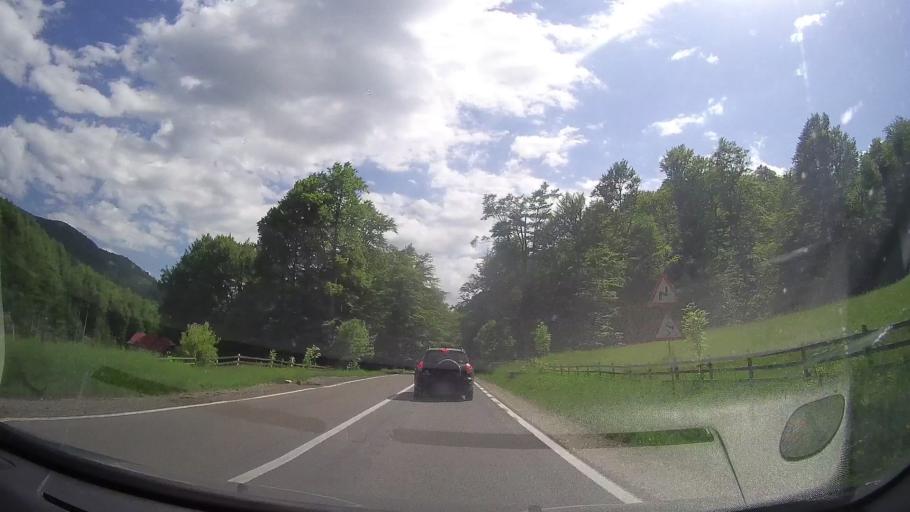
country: RO
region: Prahova
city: Maneciu
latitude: 45.4023
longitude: 25.9339
